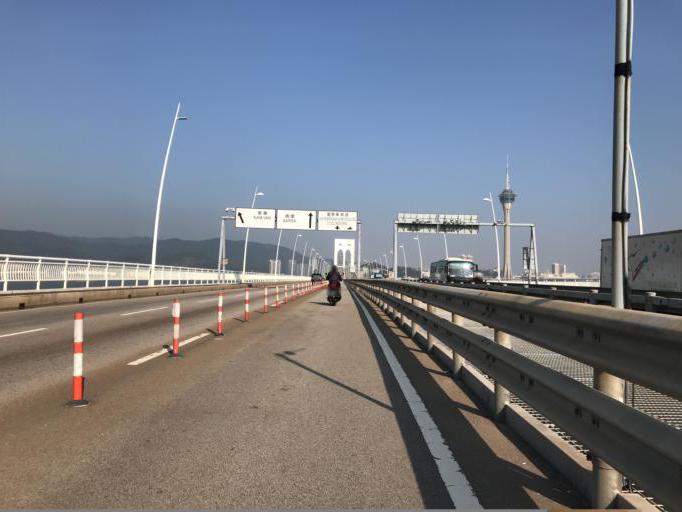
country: MO
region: Macau
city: Macau
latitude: 22.1665
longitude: 113.5390
